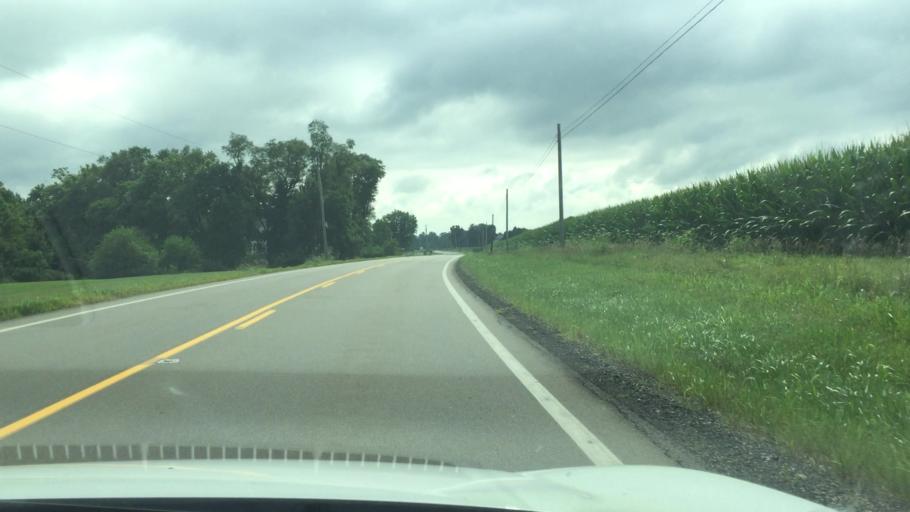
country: US
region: Ohio
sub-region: Champaign County
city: Mechanicsburg
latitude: 40.0614
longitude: -83.5837
